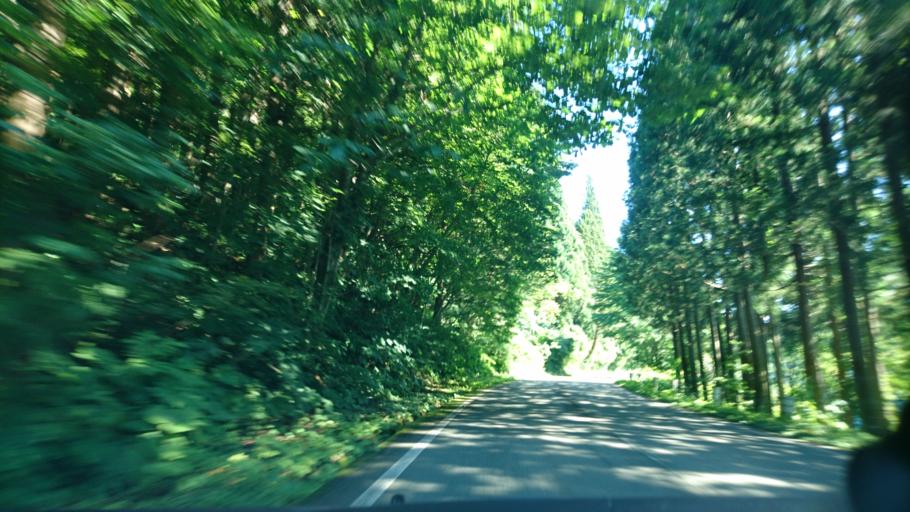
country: JP
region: Akita
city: Kakunodatemachi
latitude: 39.7345
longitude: 140.6321
